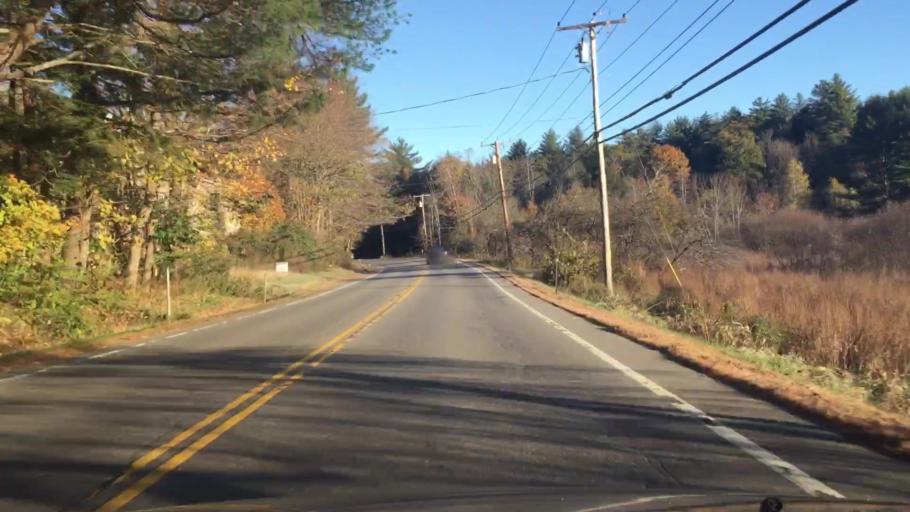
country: US
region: New Hampshire
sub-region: Cheshire County
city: Keene
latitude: 43.0073
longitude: -72.2611
